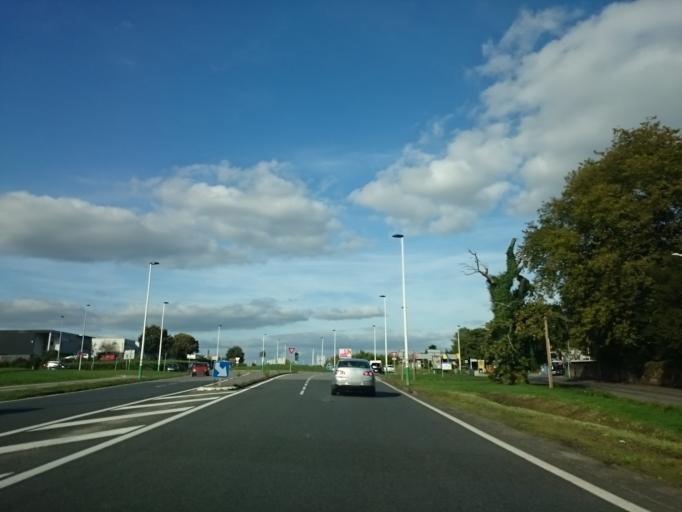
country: FR
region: Pays de la Loire
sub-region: Departement de la Loire-Atlantique
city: Saint-Herblain
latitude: 47.2263
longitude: -1.6519
